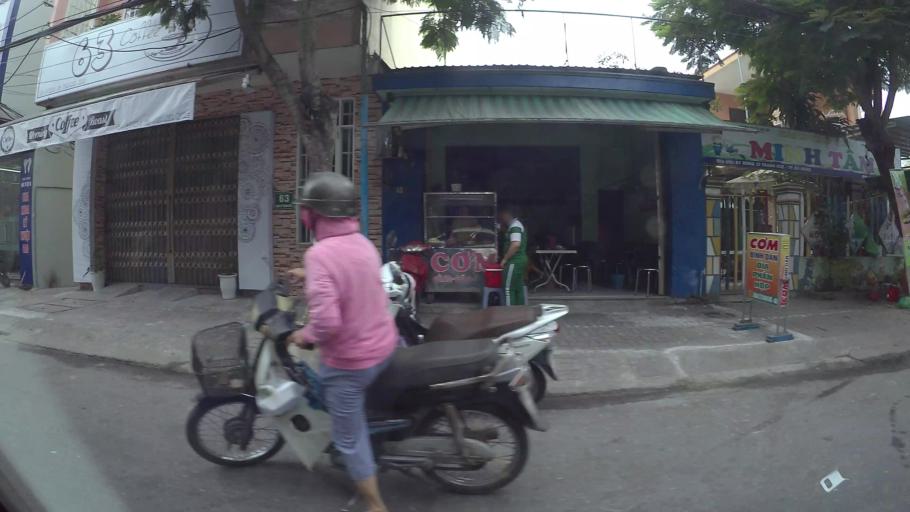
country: VN
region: Da Nang
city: Thanh Khe
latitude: 16.0731
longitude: 108.1777
